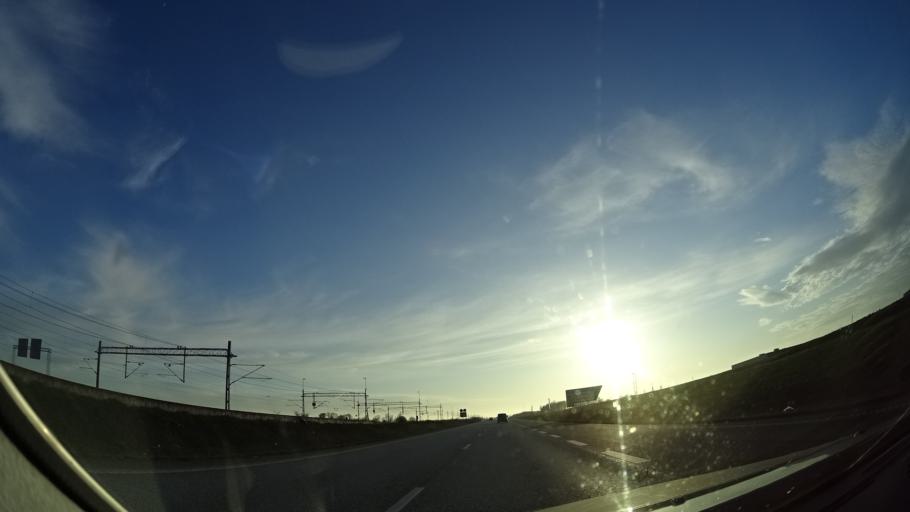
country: SE
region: Skane
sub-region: Malmo
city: Tygelsjo
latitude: 55.5475
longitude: 12.9893
